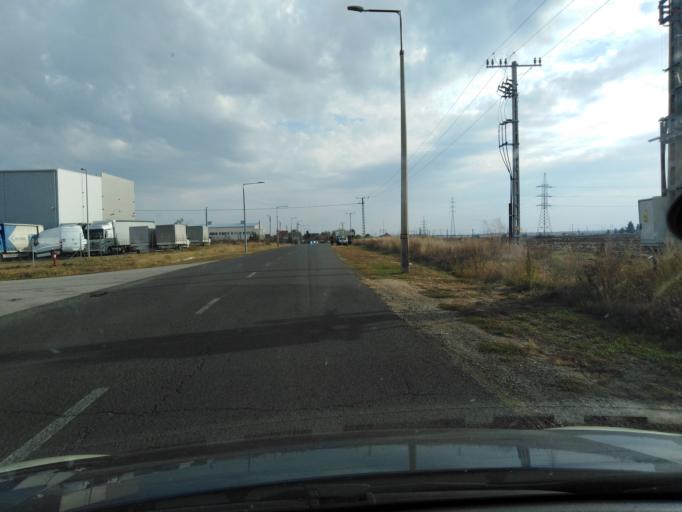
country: HU
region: Heves
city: Hatvan
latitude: 47.6654
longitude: 19.6429
